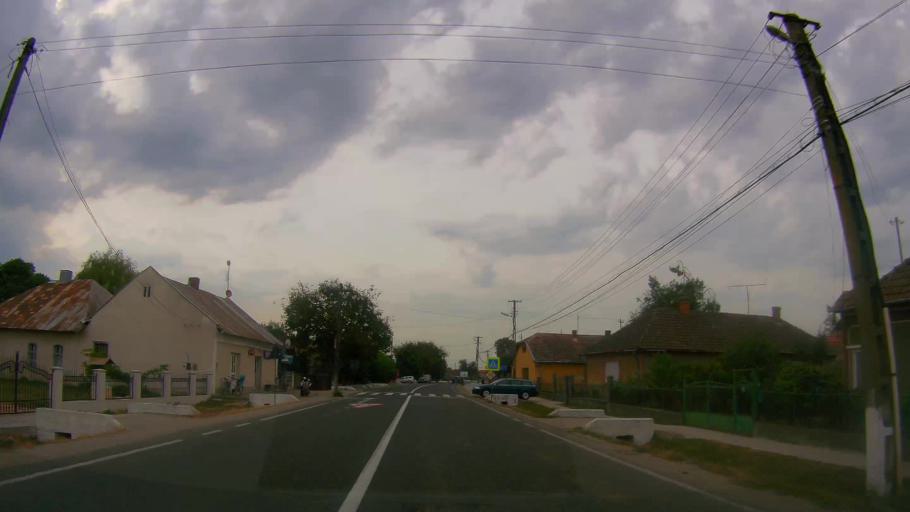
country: RO
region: Satu Mare
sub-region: Comuna Acas
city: Acas
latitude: 47.5375
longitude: 22.7836
